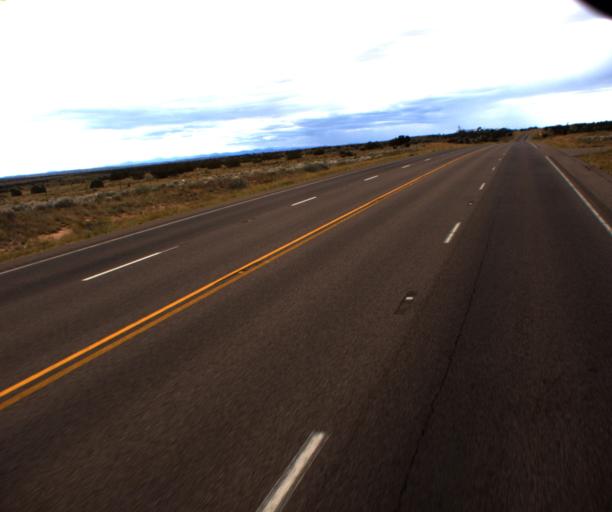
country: US
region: Arizona
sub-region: Navajo County
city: Snowflake
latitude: 34.5798
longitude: -110.0843
